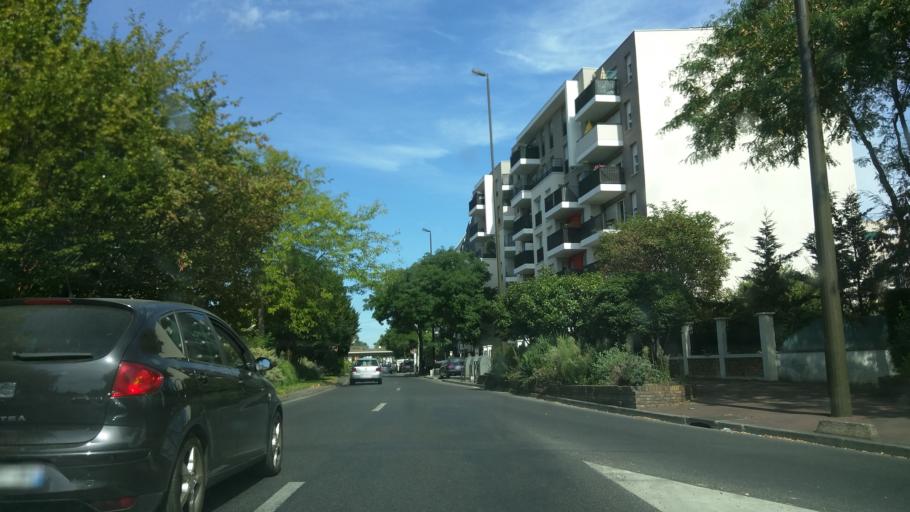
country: FR
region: Ile-de-France
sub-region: Departement des Yvelines
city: Sartrouville
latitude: 48.9416
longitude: 2.2069
